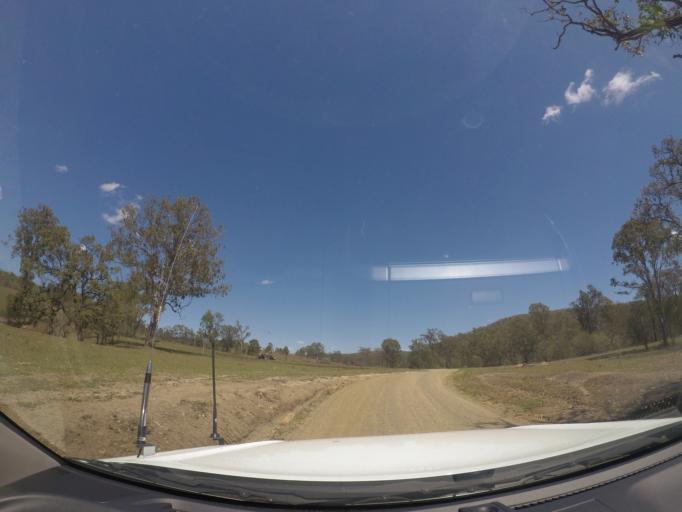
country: AU
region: Queensland
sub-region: Logan
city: Cedar Vale
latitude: -27.8572
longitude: 152.8685
